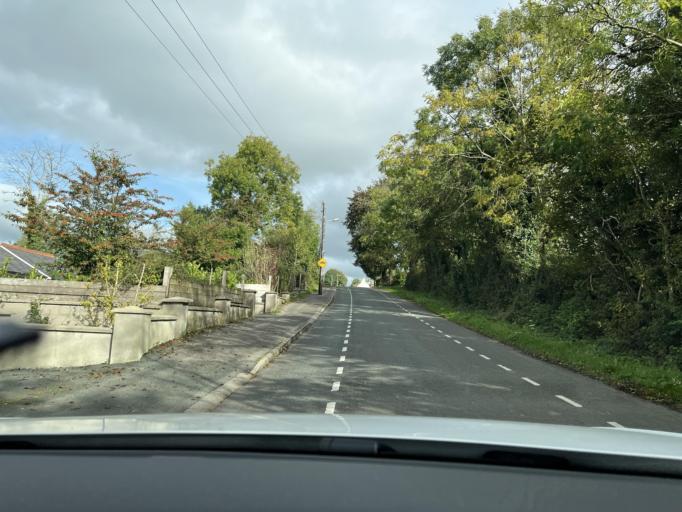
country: IE
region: Connaught
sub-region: County Leitrim
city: Carrick-on-Shannon
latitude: 53.9513
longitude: -8.0787
